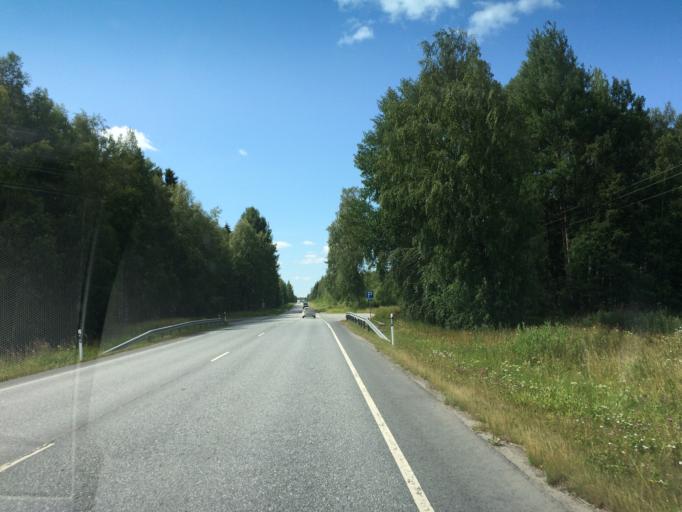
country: FI
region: Pirkanmaa
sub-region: Lounais-Pirkanmaa
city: Kiikoinen
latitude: 61.4852
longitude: 22.6525
